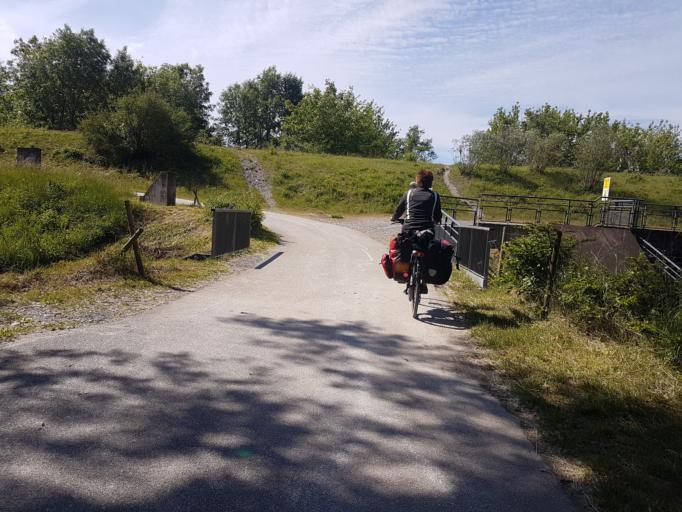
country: FR
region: Rhone-Alpes
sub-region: Departement de l'Ardeche
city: La Voulte-sur-Rhone
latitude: 44.7731
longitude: 4.7673
